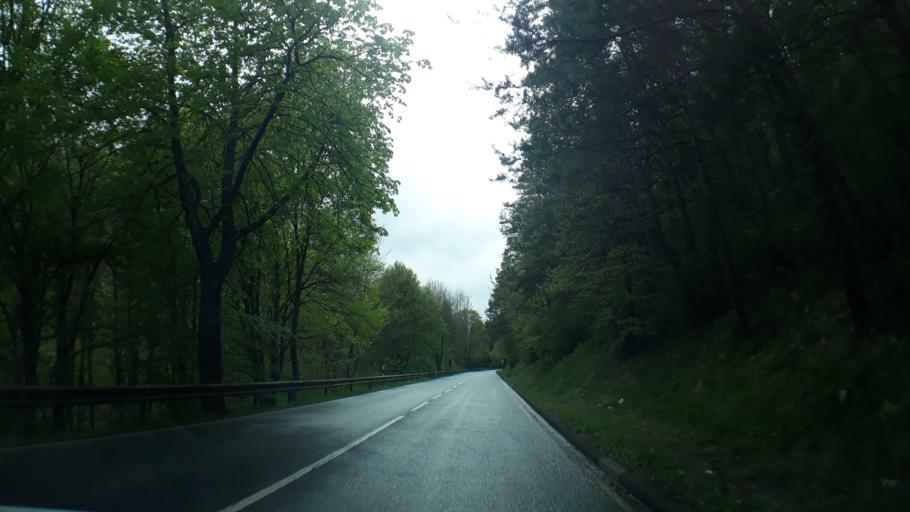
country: DE
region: North Rhine-Westphalia
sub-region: Regierungsbezirk Koln
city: Kall
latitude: 50.5192
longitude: 6.5566
